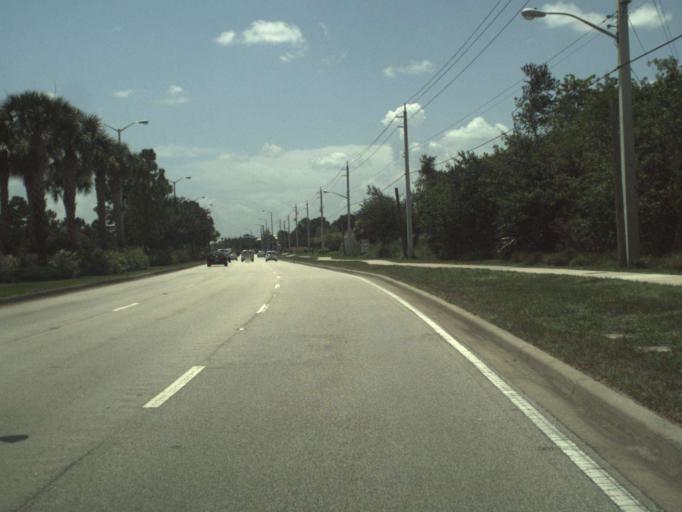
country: US
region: Florida
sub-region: Saint Lucie County
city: Port Saint Lucie
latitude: 27.2648
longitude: -80.3954
